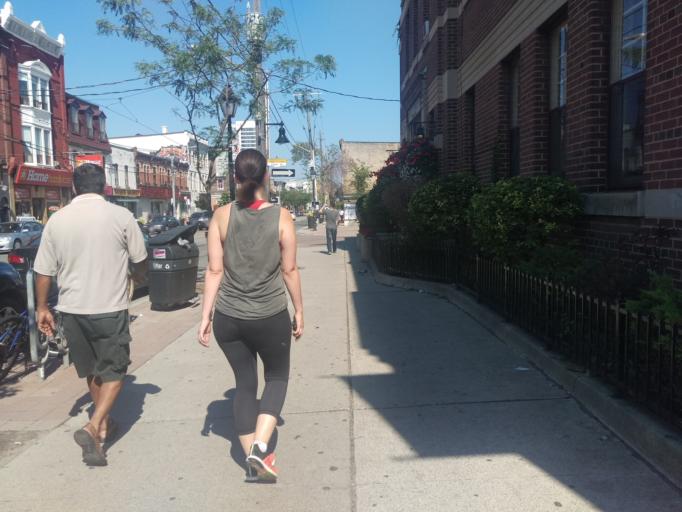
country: CA
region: Ontario
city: Toronto
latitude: 43.6412
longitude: -79.4335
